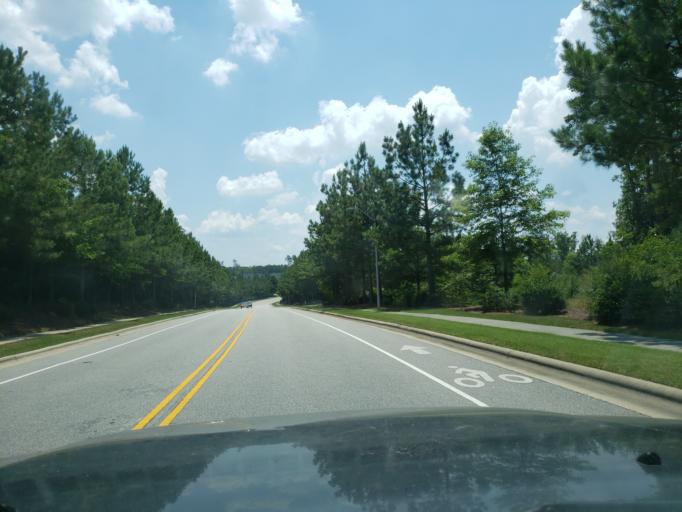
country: US
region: North Carolina
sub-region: Wake County
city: Green Level
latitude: 35.8396
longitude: -78.9141
